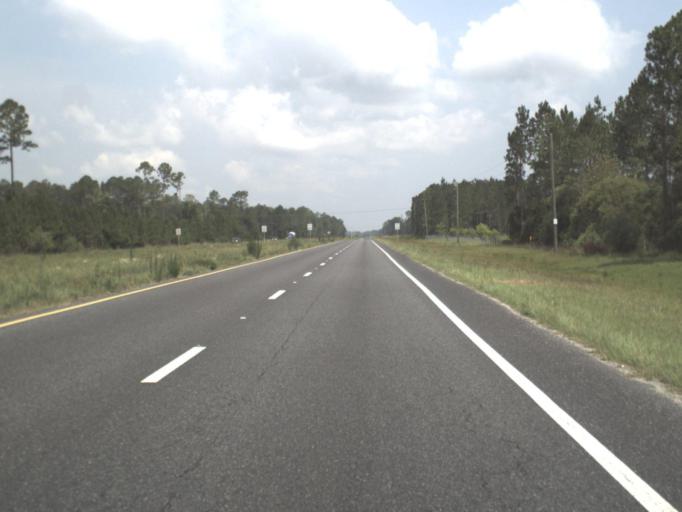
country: US
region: Florida
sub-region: Levy County
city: Bronson
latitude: 29.4535
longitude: -82.6505
